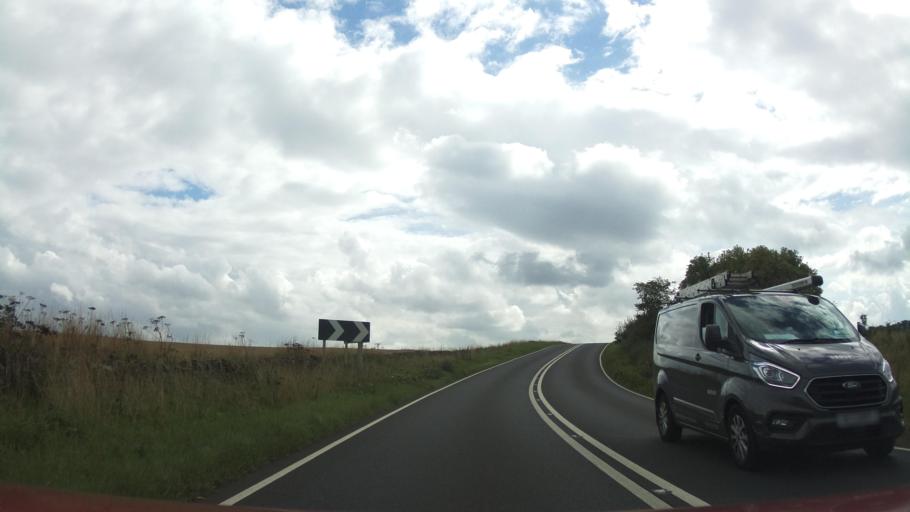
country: GB
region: England
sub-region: Northumberland
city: Corbridge
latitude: 55.0305
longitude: -2.0293
